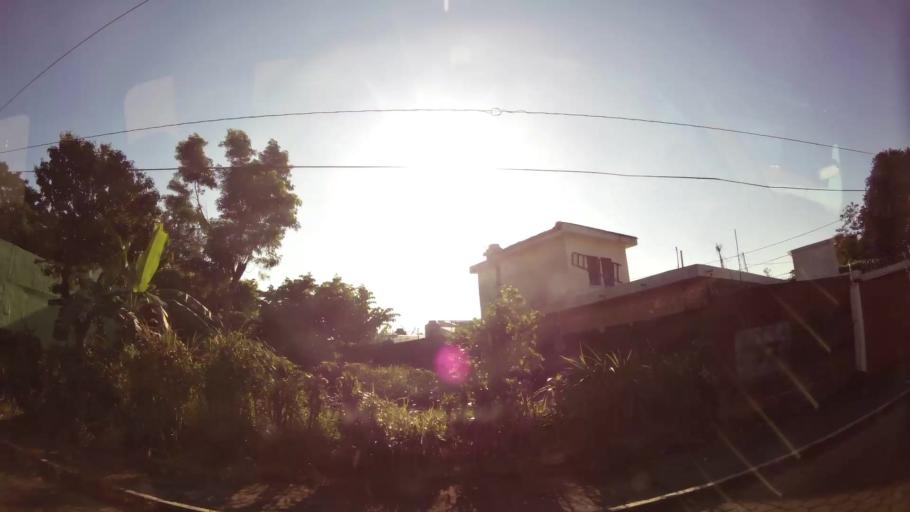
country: GT
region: Suchitepeque
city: Mazatenango
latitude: 14.5312
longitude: -91.5166
